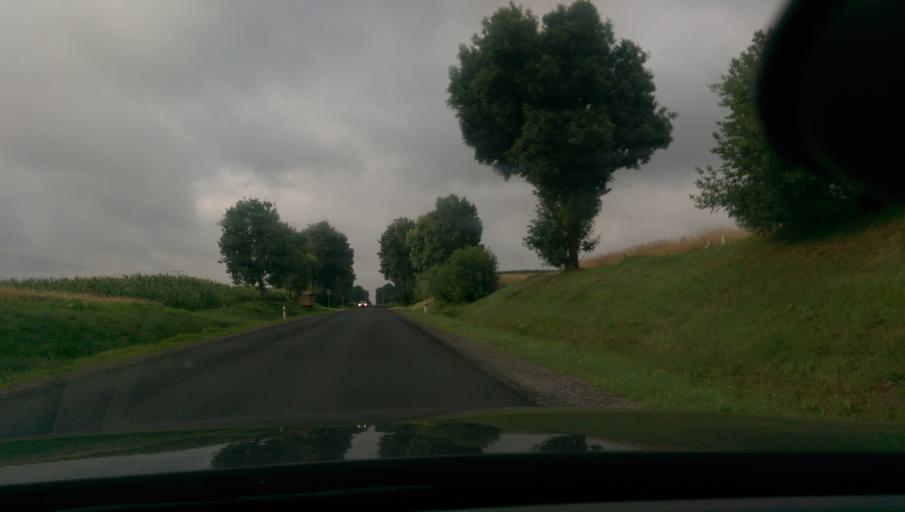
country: PL
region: Masovian Voivodeship
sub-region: Powiat przasnyski
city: Przasnysz
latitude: 53.0866
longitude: 20.8549
